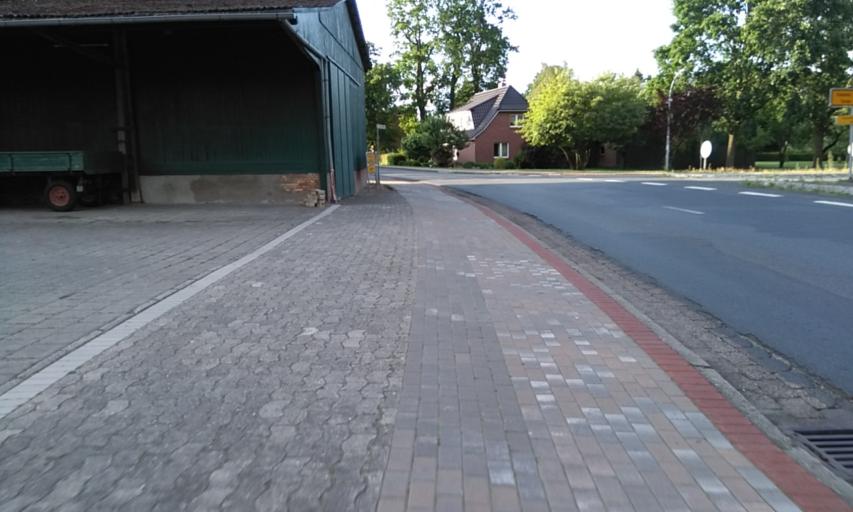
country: DE
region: Lower Saxony
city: Anderlingen
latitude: 53.3743
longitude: 9.3024
